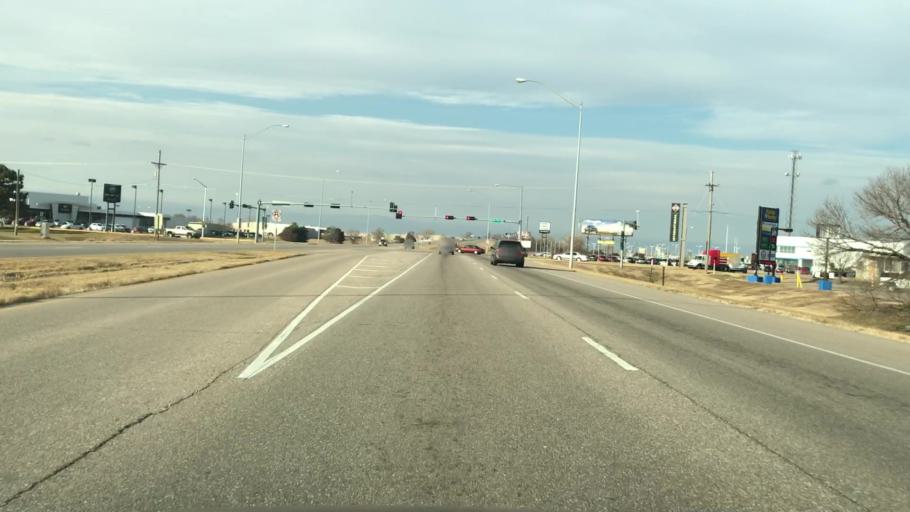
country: US
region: Nebraska
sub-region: Hall County
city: Grand Island
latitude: 40.9014
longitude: -98.3808
